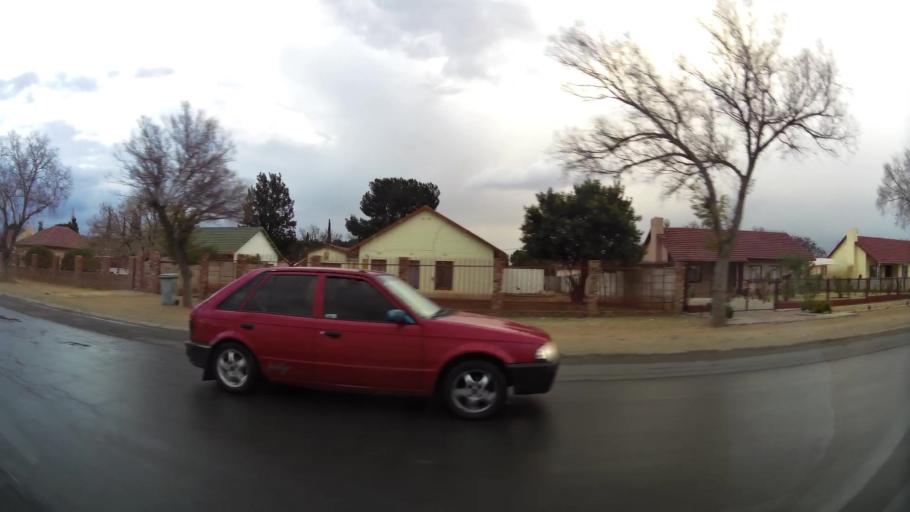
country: ZA
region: Orange Free State
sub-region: Lejweleputswa District Municipality
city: Welkom
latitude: -27.9749
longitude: 26.7648
